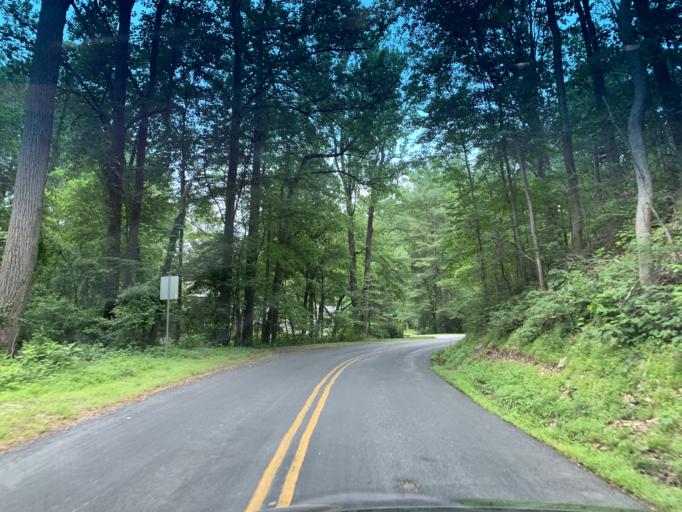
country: US
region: Maryland
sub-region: Harford County
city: Jarrettsville
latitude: 39.6257
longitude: -76.5020
